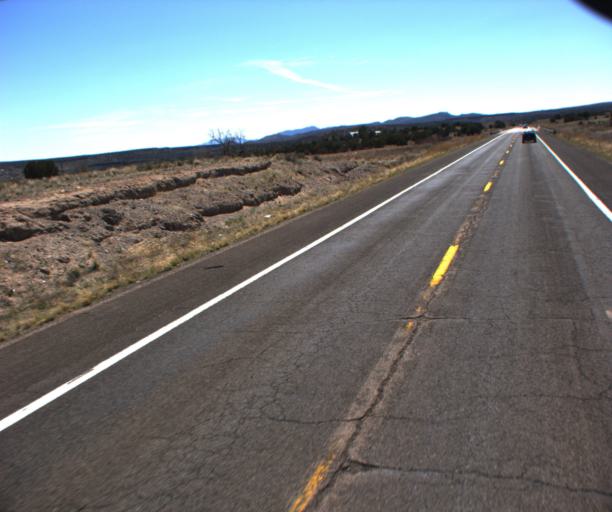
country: US
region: Arizona
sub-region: Mohave County
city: Peach Springs
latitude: 35.4626
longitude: -113.6094
